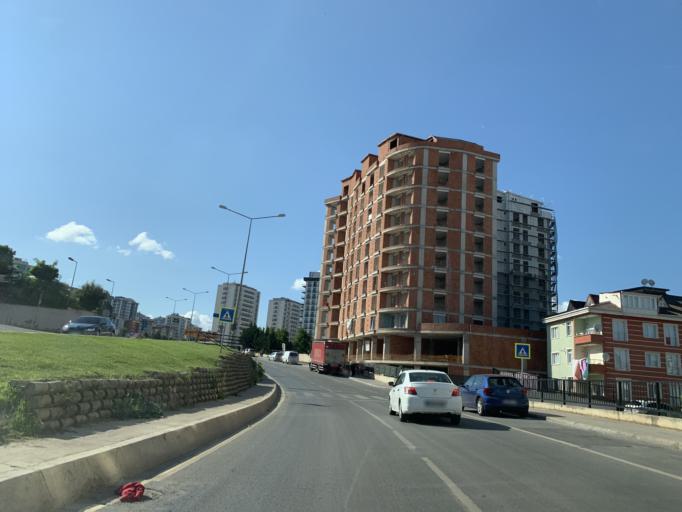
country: TR
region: Istanbul
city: Pendik
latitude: 40.8874
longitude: 29.2650
